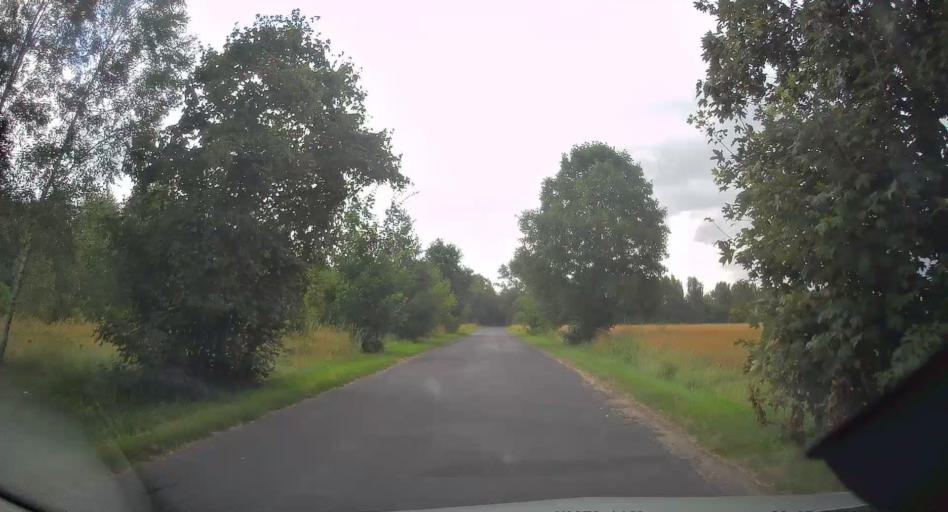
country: PL
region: Lodz Voivodeship
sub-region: Powiat rawski
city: Rawa Mazowiecka
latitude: 51.7415
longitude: 20.1890
